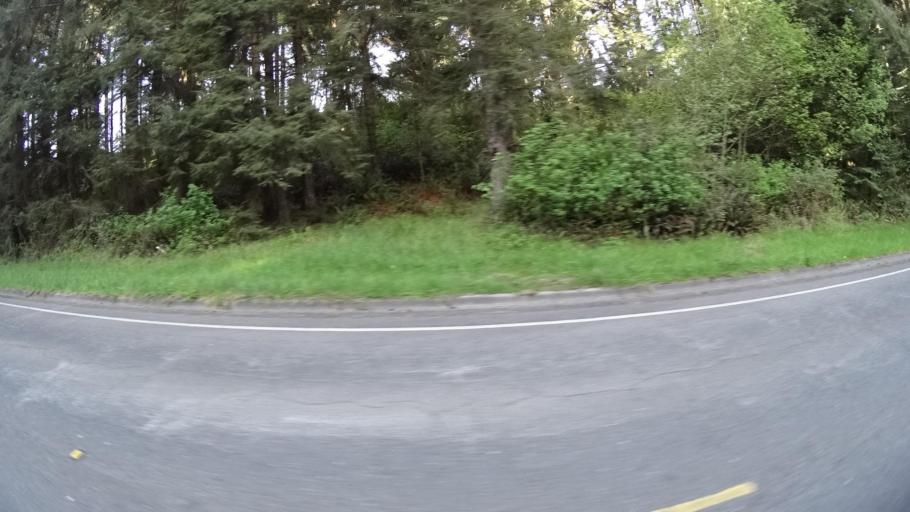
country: US
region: California
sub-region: Humboldt County
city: Humboldt Hill
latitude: 40.7238
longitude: -124.2011
